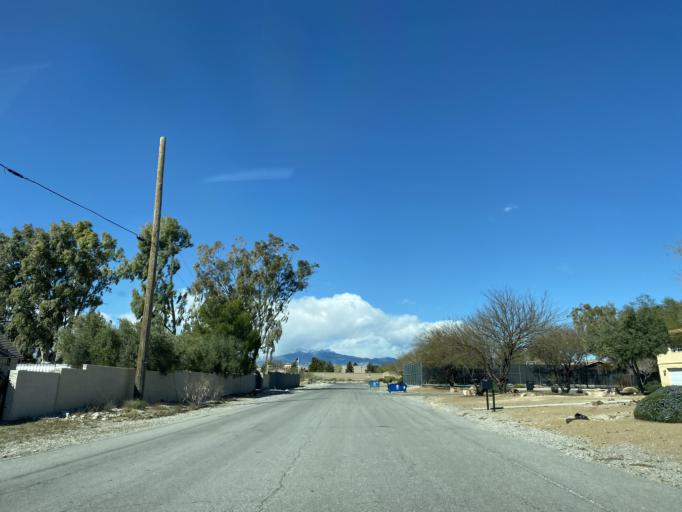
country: US
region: Nevada
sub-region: Clark County
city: North Las Vegas
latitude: 36.3267
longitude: -115.2856
